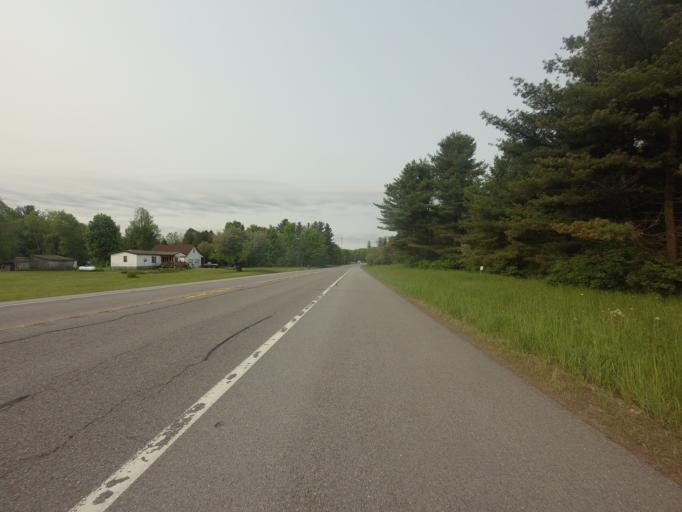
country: US
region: New York
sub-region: Jefferson County
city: Carthage
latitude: 44.0443
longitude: -75.5648
